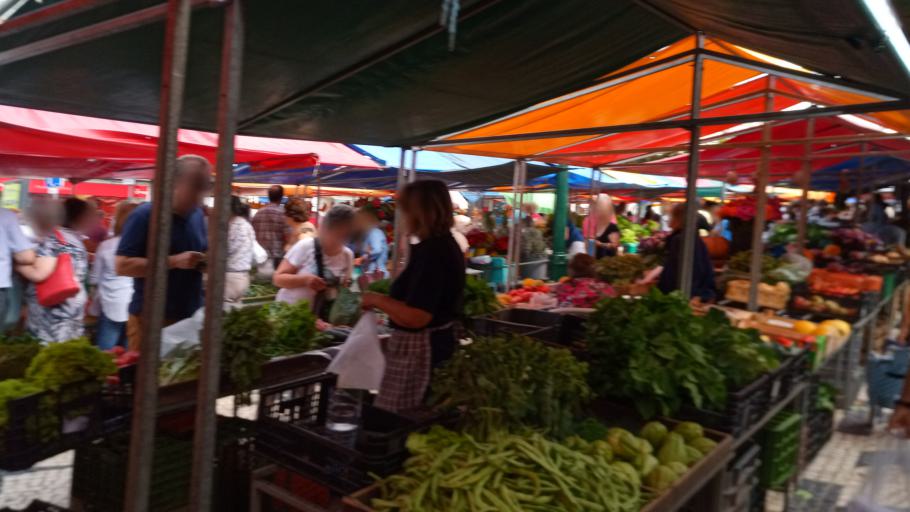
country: PT
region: Leiria
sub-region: Caldas da Rainha
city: Caldas da Rainha
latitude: 39.4038
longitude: -9.1338
